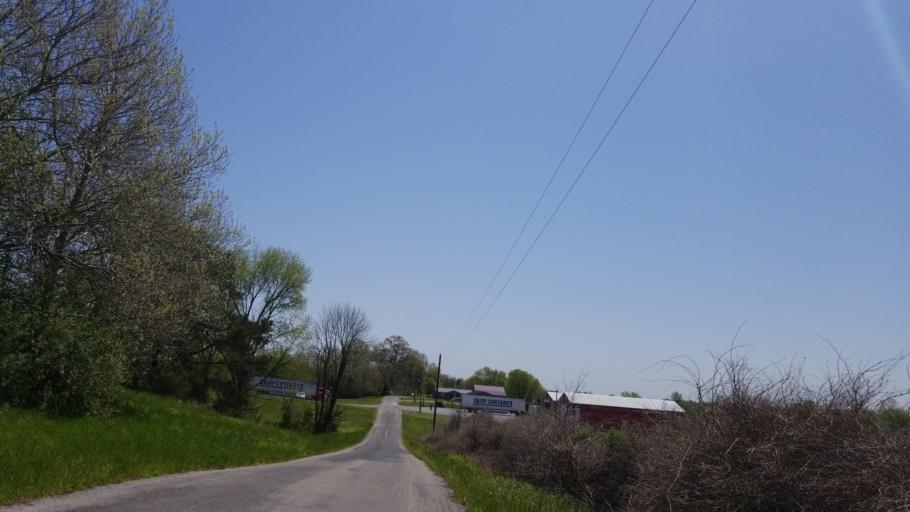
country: US
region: Illinois
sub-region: Saline County
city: Harrisburg
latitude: 37.8495
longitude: -88.6010
